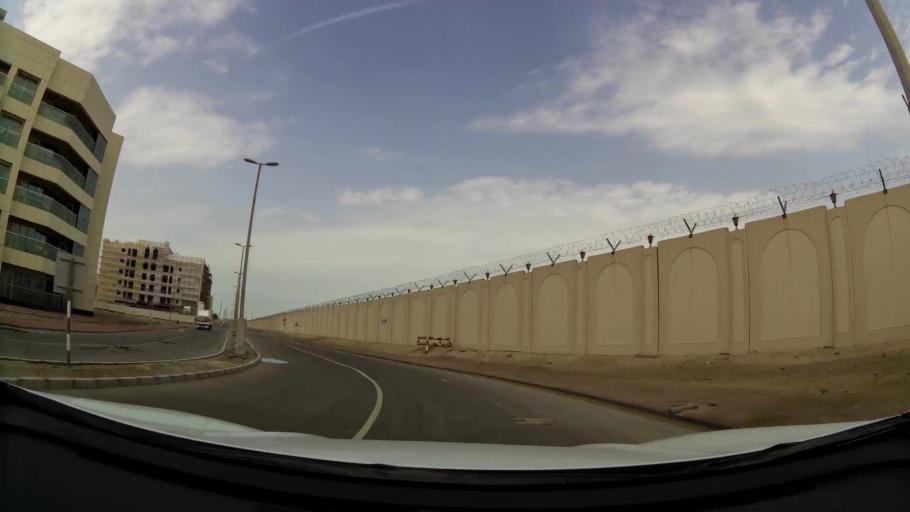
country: AE
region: Abu Dhabi
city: Abu Dhabi
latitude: 24.4176
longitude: 54.4687
